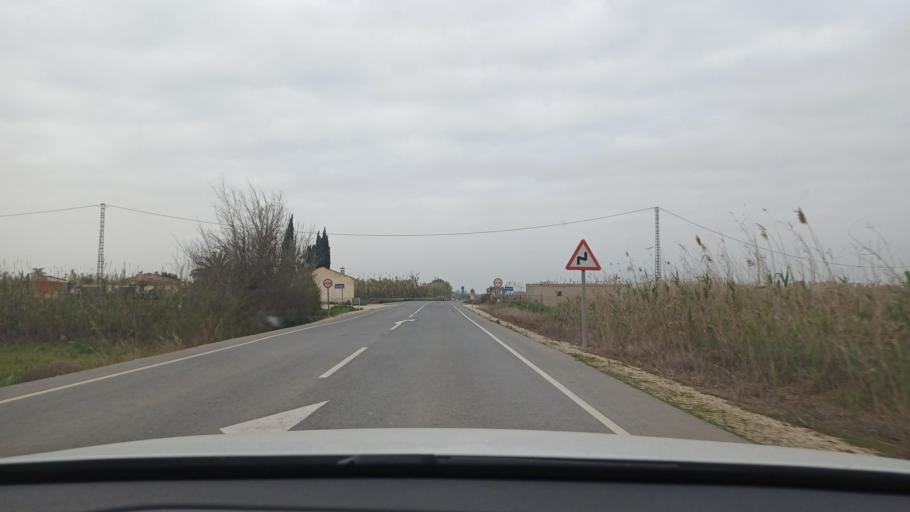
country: ES
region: Valencia
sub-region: Provincia de Alicante
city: Daya Vieja
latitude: 38.1461
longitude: -0.7268
